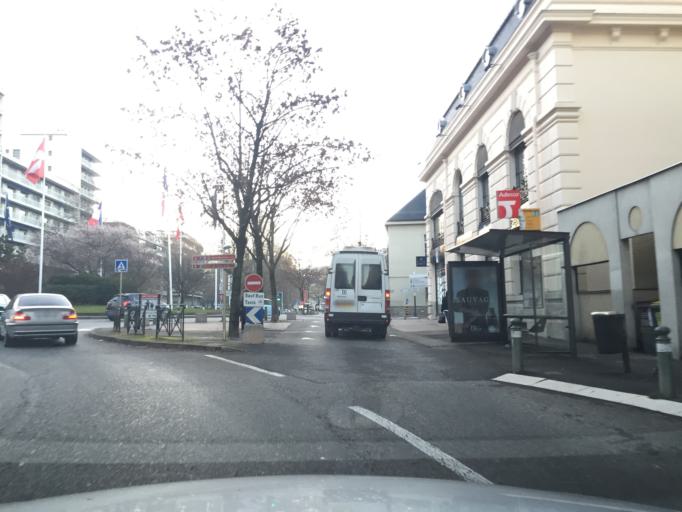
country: FR
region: Rhone-Alpes
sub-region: Departement de la Savoie
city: Chambery
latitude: 45.5709
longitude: 5.9173
